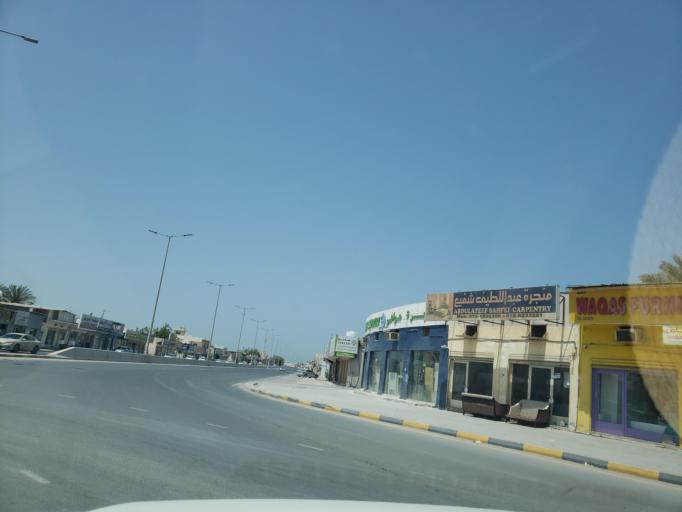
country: AE
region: Ra's al Khaymah
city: Ras al-Khaimah
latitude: 25.8150
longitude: 55.9759
